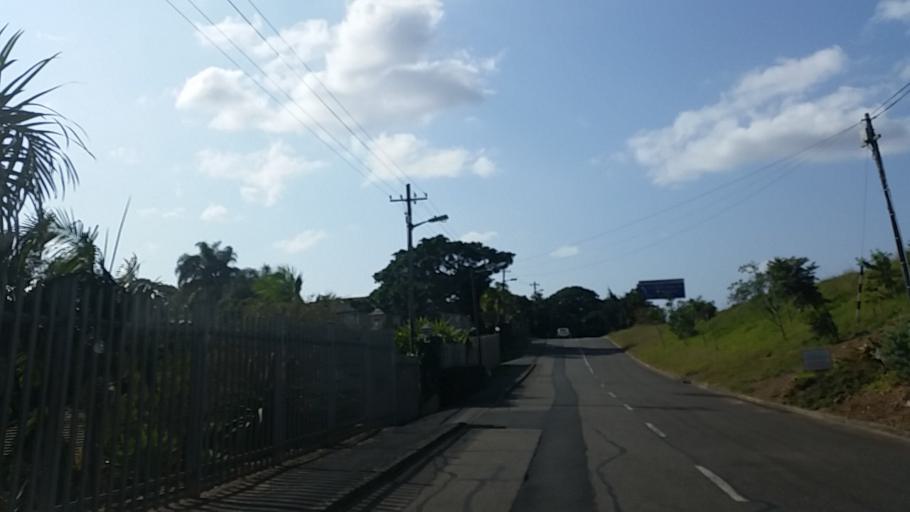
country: ZA
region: KwaZulu-Natal
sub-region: eThekwini Metropolitan Municipality
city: Berea
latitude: -29.8347
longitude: 30.9108
